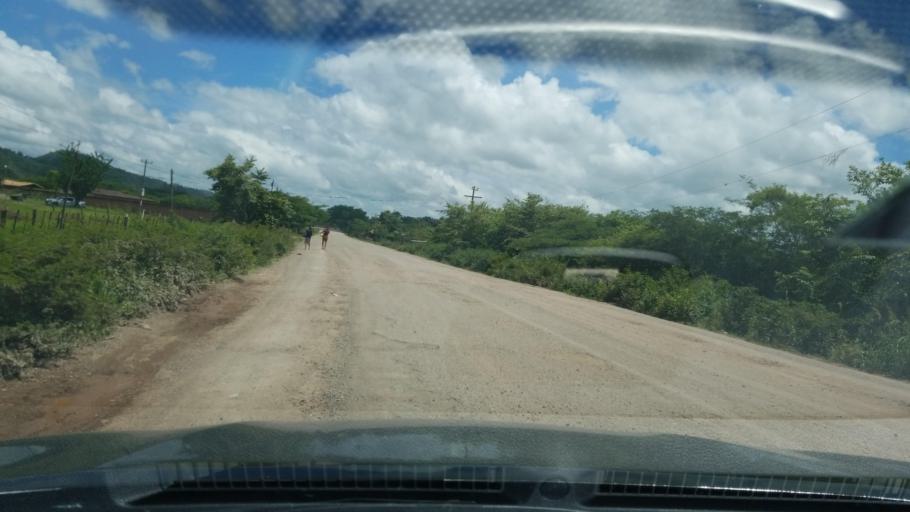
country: HN
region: Francisco Morazan
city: Talanga
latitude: 14.3667
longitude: -87.0533
